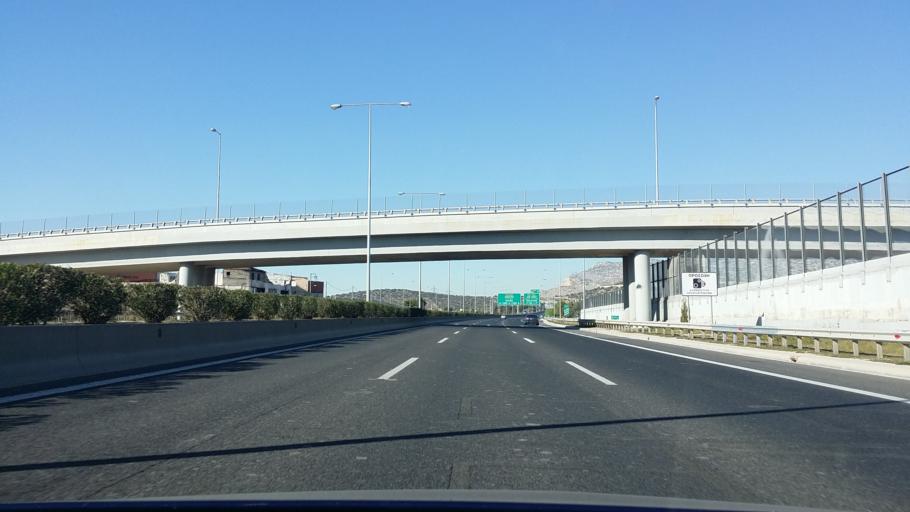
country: GR
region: Attica
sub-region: Nomarchia Dytikis Attikis
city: Ano Liosia
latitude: 38.0750
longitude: 23.6863
